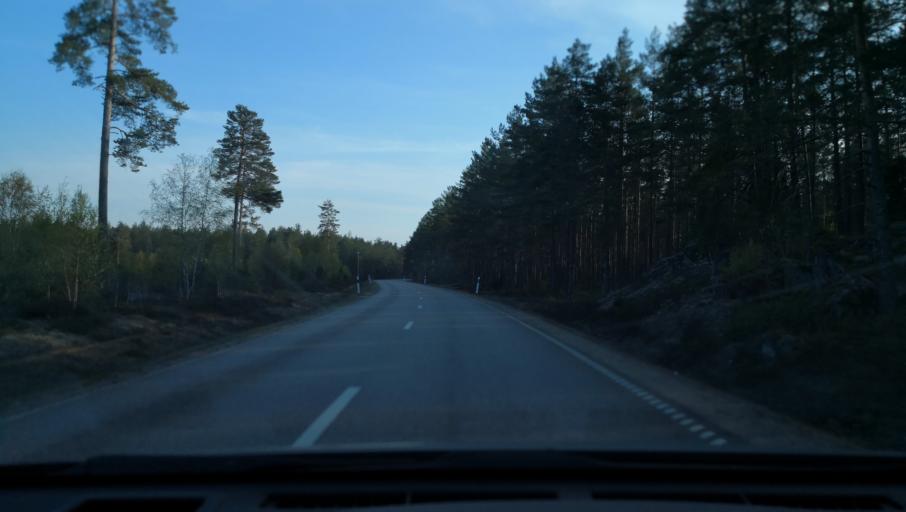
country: SE
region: Uppsala
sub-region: Heby Kommun
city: Heby
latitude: 60.0287
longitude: 16.8525
